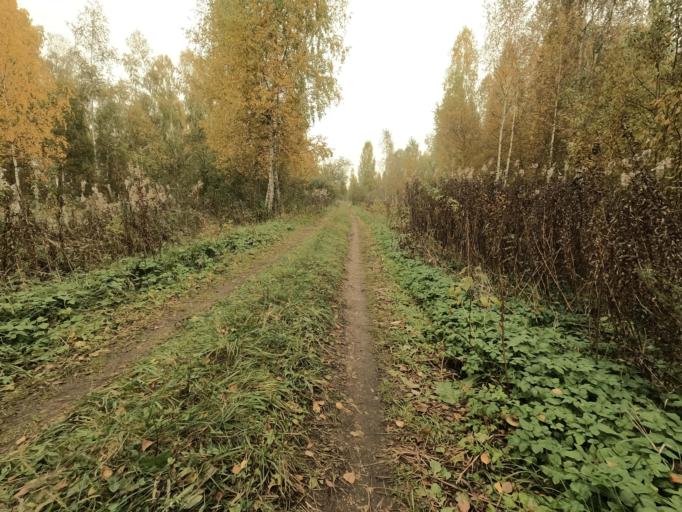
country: RU
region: Novgorod
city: Pankovka
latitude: 58.8745
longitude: 30.9392
